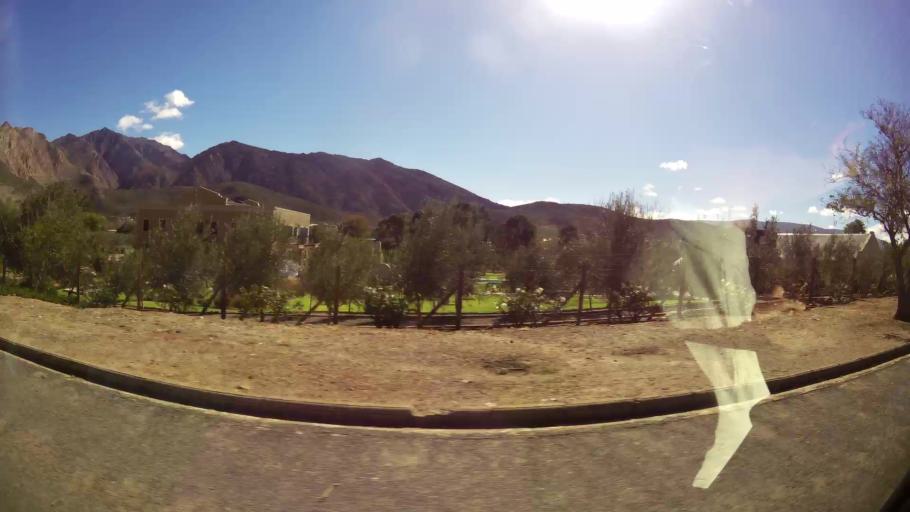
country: ZA
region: Western Cape
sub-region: Cape Winelands District Municipality
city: Ashton
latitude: -33.7940
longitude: 20.1170
